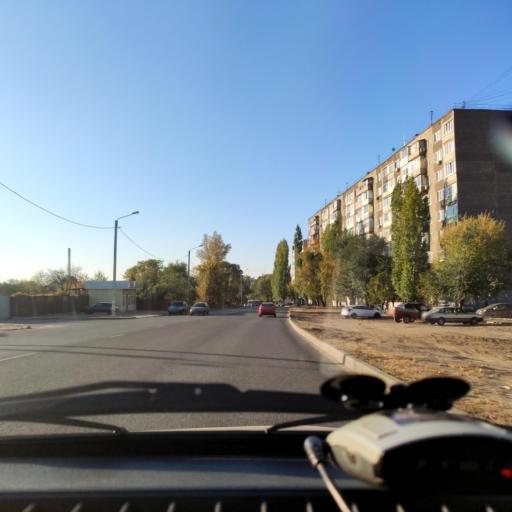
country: RU
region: Voronezj
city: Podgornoye
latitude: 51.6994
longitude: 39.1487
